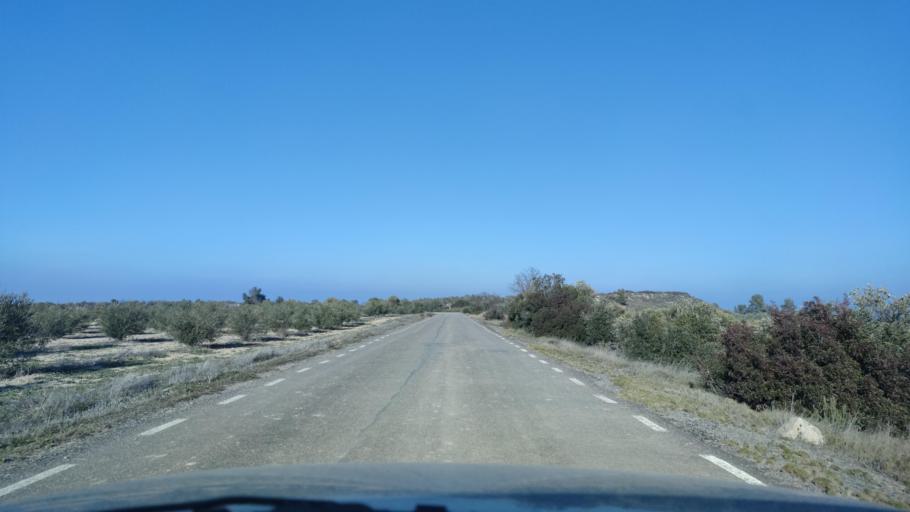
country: ES
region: Catalonia
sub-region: Provincia de Lleida
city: Torrebesses
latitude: 41.4231
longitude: 0.5716
